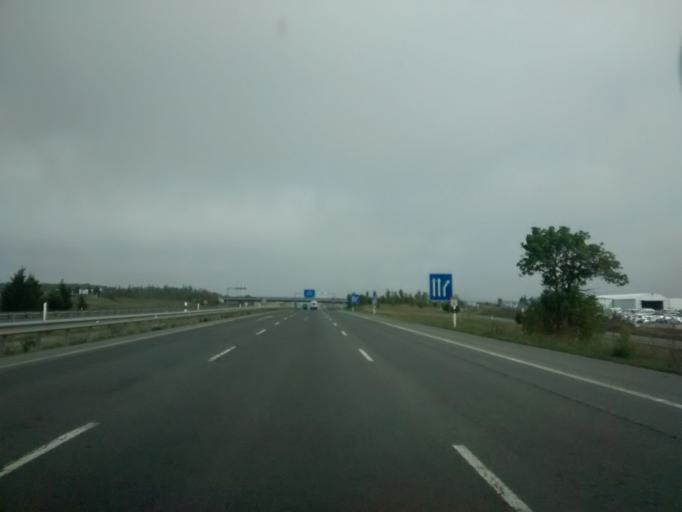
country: ES
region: Basque Country
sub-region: Provincia de Alava
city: Gasteiz / Vitoria
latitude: 42.8900
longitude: -2.6530
